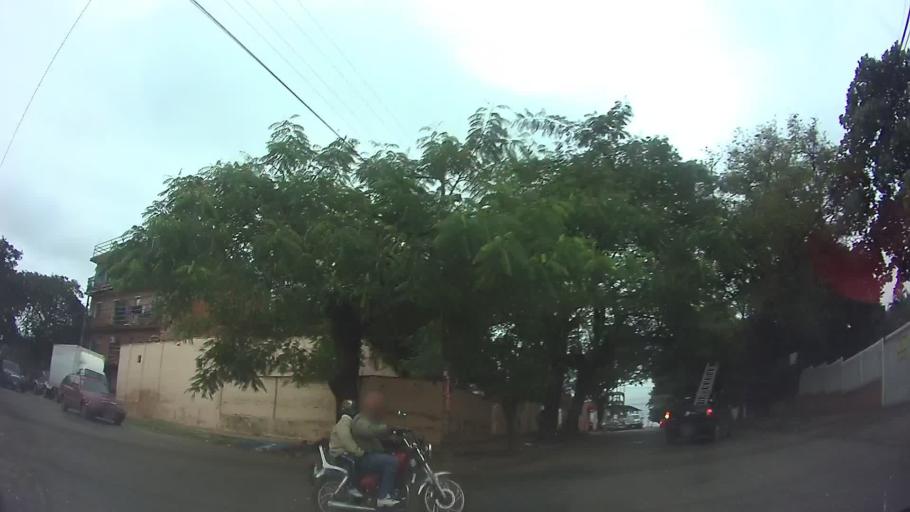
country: PY
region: Asuncion
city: Asuncion
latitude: -25.3157
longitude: -57.6206
